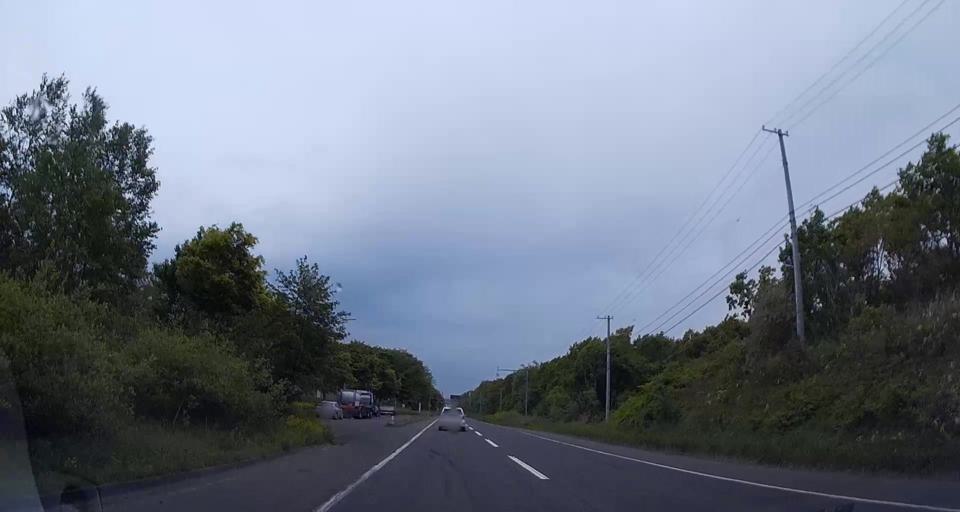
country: JP
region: Hokkaido
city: Tomakomai
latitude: 42.6945
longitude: 141.7351
